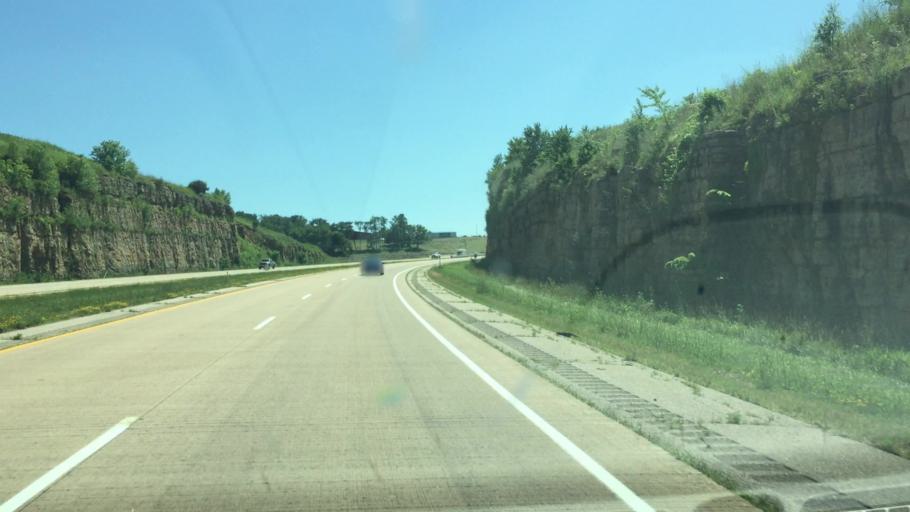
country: US
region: Wisconsin
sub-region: Iowa County
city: Mineral Point
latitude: 42.8701
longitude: -90.1937
